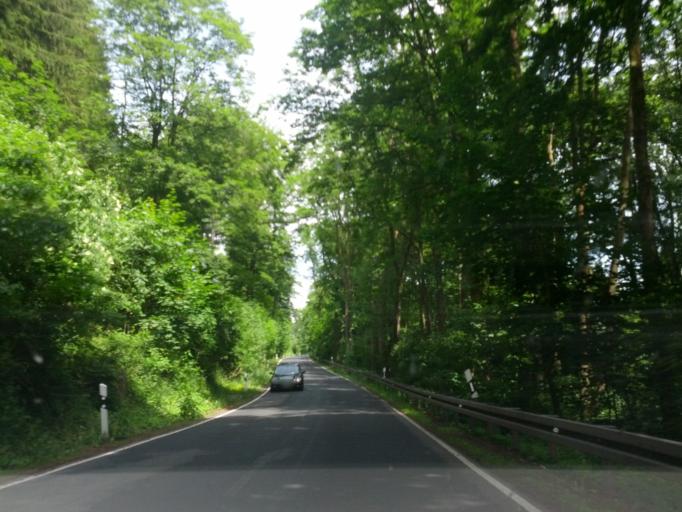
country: DE
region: Thuringia
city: Finsterbergen
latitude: 50.8441
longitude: 10.6086
